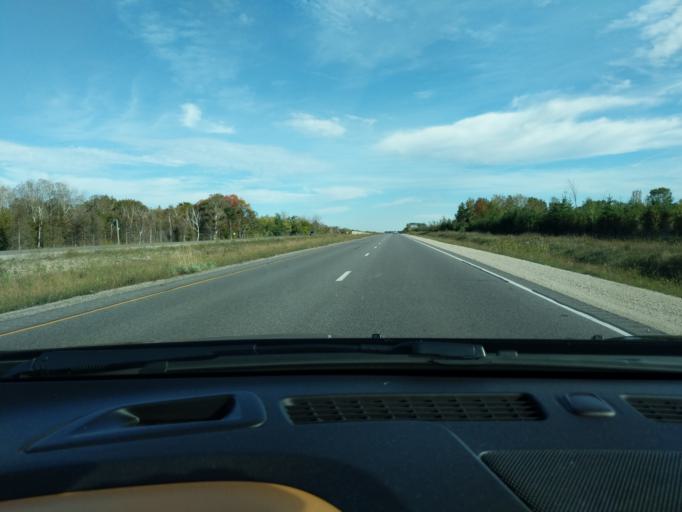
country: CA
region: Ontario
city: Collingwood
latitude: 44.4807
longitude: -80.1667
